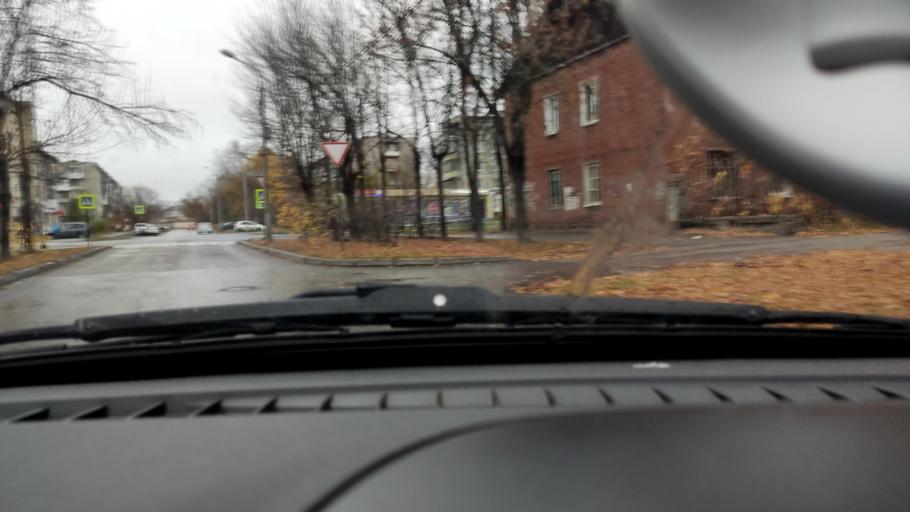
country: RU
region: Perm
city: Kultayevo
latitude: 57.9983
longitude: 55.9416
